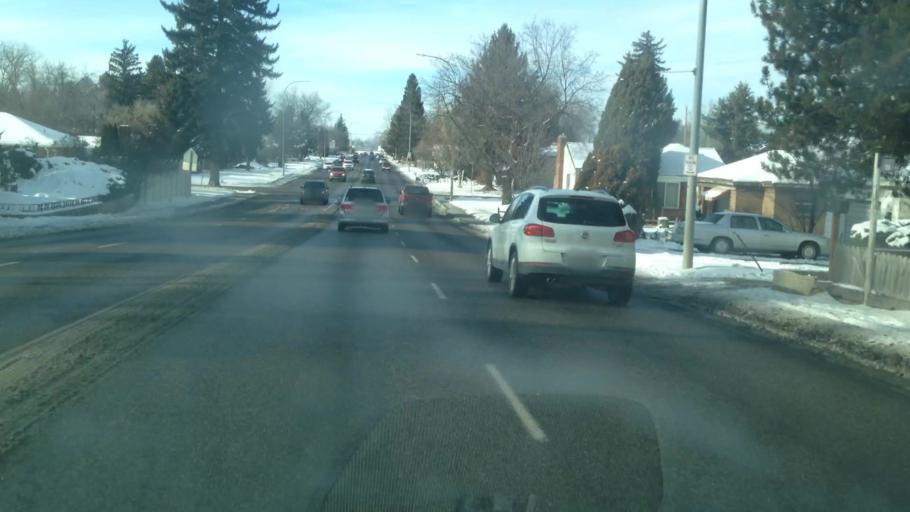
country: US
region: Idaho
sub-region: Bonneville County
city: Idaho Falls
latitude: 43.4826
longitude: -112.0350
